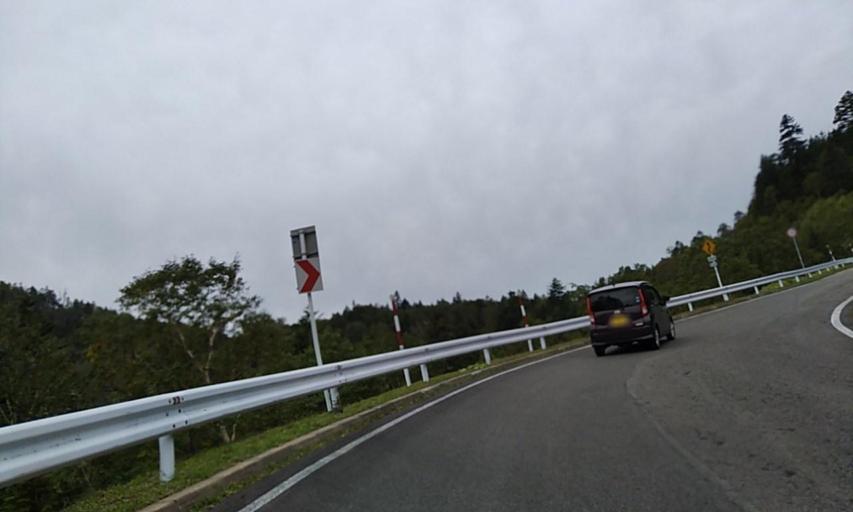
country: JP
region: Hokkaido
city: Bihoro
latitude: 43.5677
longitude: 144.2299
